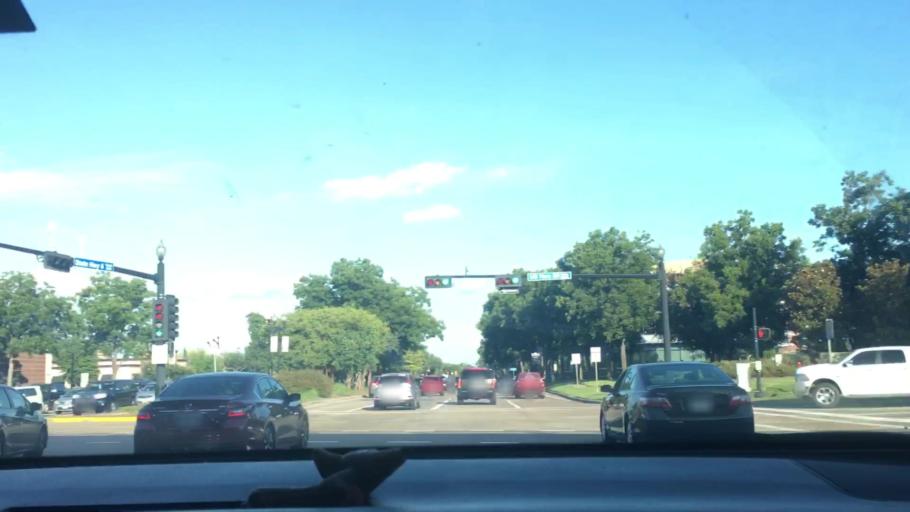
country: US
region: Texas
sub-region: Fort Bend County
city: Sugar Land
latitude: 29.5982
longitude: -95.6224
